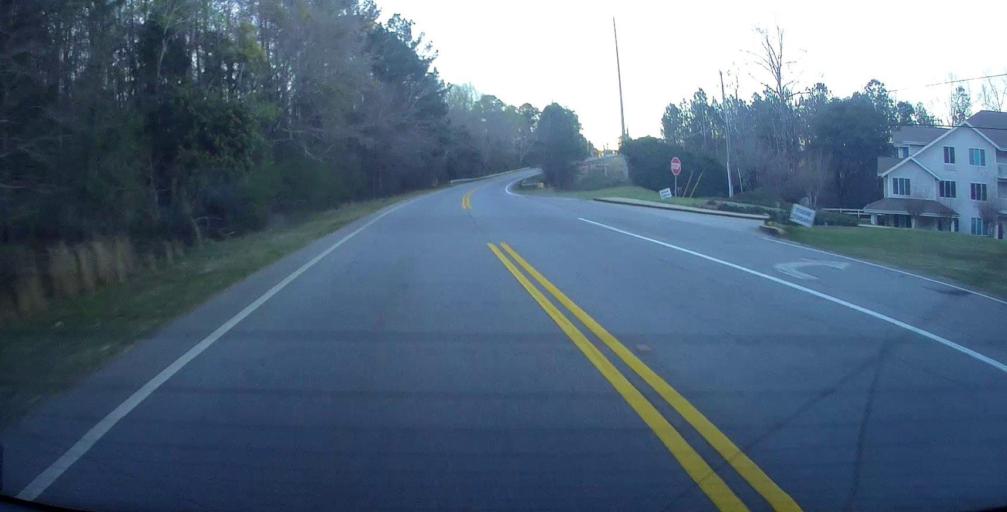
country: US
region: Alabama
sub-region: Russell County
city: Phenix City
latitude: 32.5400
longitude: -84.9964
